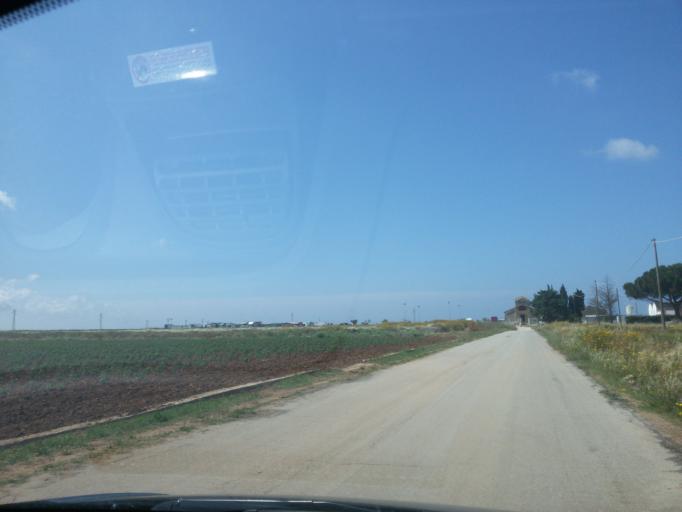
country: IT
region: Apulia
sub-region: Provincia di Brindisi
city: Brindisi
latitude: 40.6587
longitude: 17.8516
